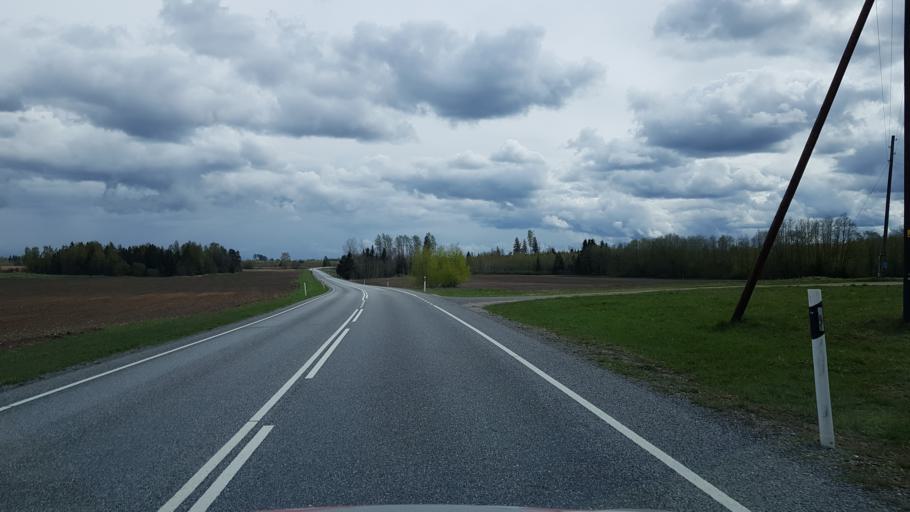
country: EE
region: Laeaene-Virumaa
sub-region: Rakke vald
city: Rakke
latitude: 59.0129
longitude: 26.2510
